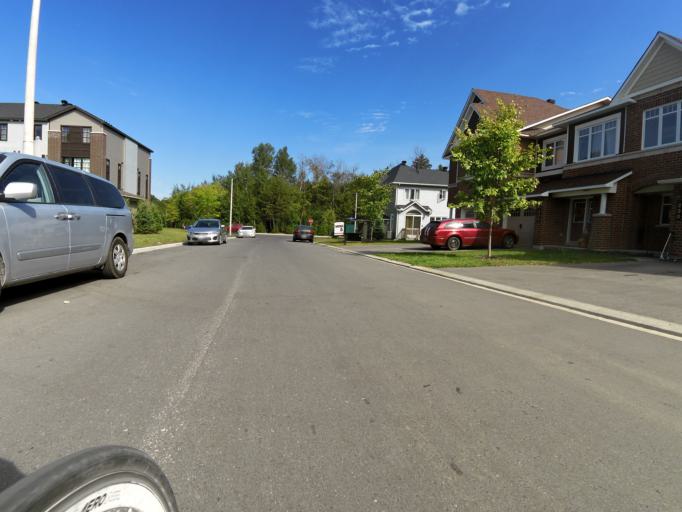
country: CA
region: Ontario
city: Bells Corners
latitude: 45.2720
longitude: -75.7360
